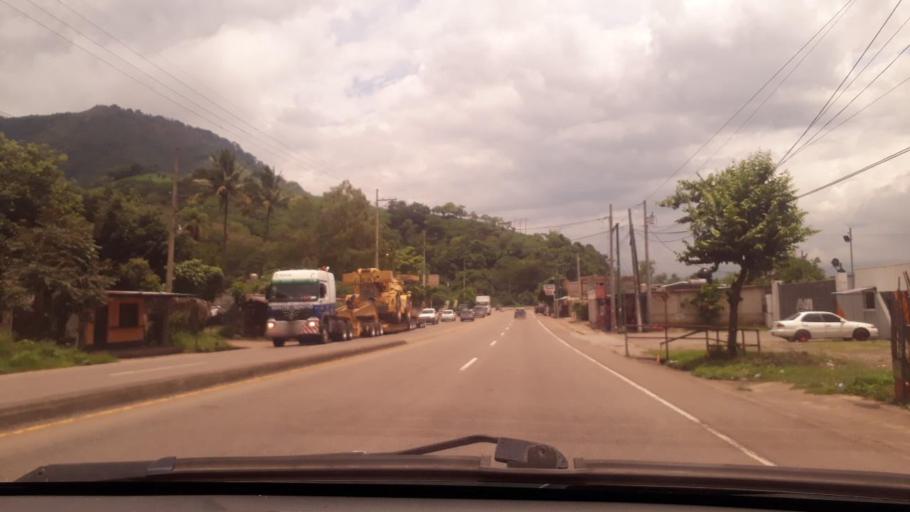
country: GT
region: Santa Rosa
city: Cuilapa
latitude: 14.2526
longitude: -90.2652
